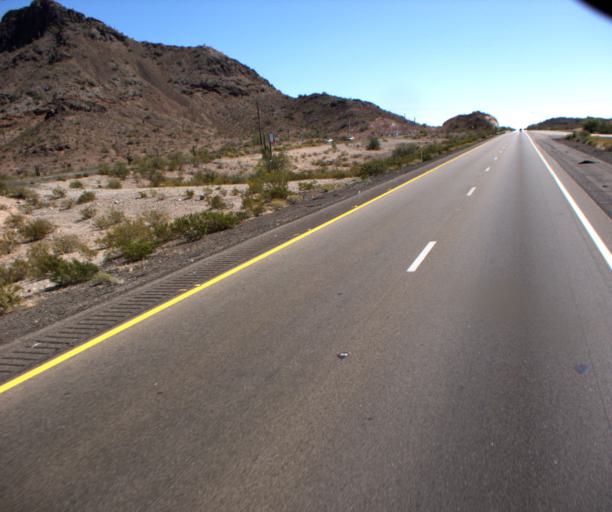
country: US
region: Arizona
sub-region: La Paz County
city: Salome
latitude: 33.6123
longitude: -113.6437
